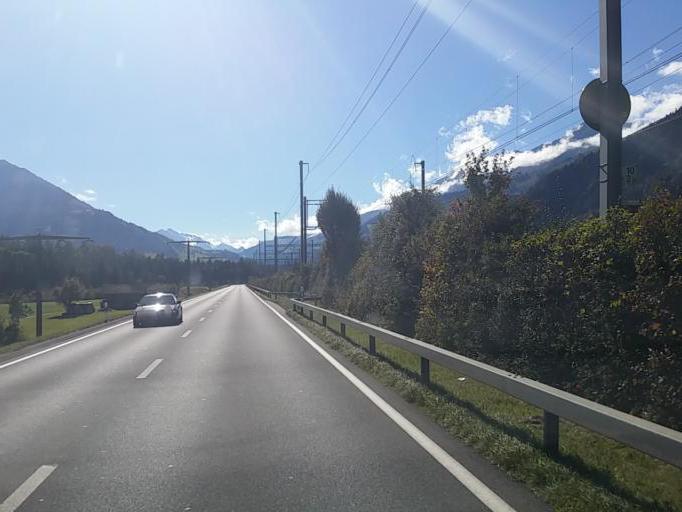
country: CH
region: Bern
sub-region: Frutigen-Niedersimmental District
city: Frutigen
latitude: 46.6131
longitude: 7.6750
